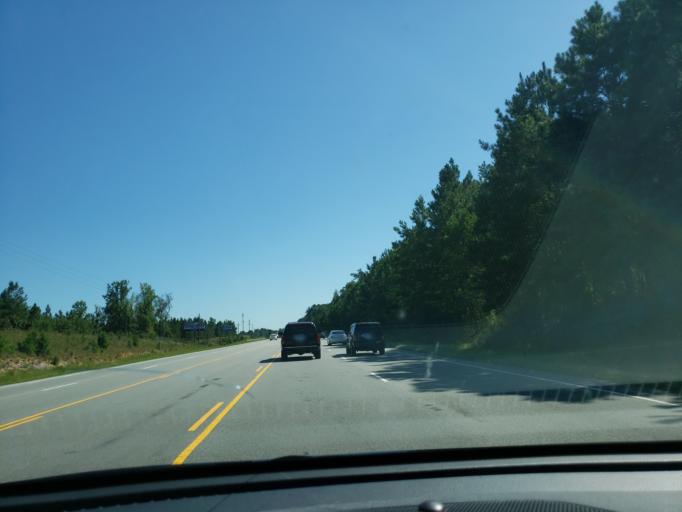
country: US
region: North Carolina
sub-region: Lee County
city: Broadway
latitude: 35.3581
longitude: -79.1098
